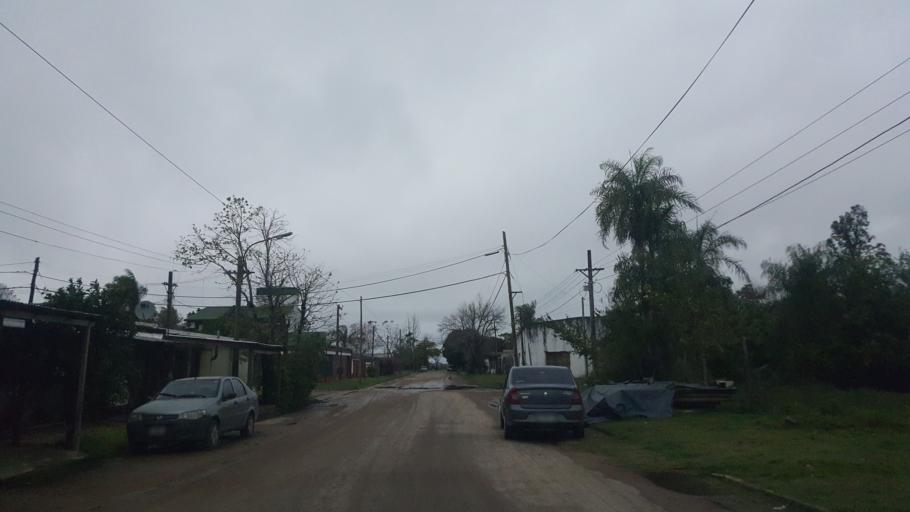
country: AR
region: Corrientes
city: Ituzaingo
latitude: -27.5923
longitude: -56.6891
